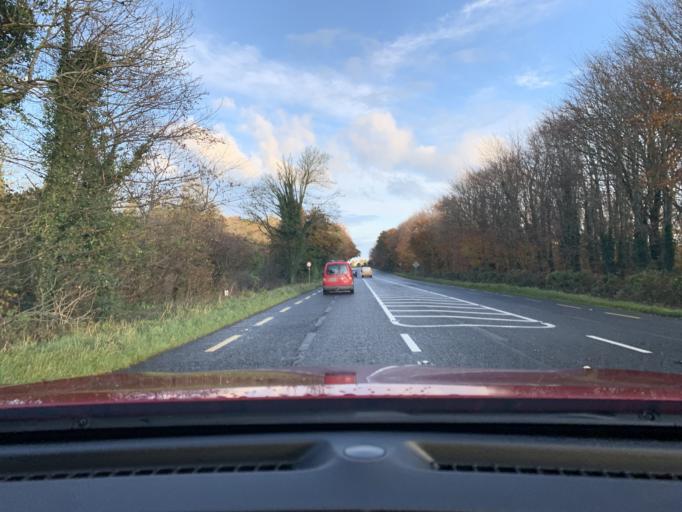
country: IE
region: Connaught
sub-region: Sligo
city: Sligo
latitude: 54.3798
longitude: -8.5289
